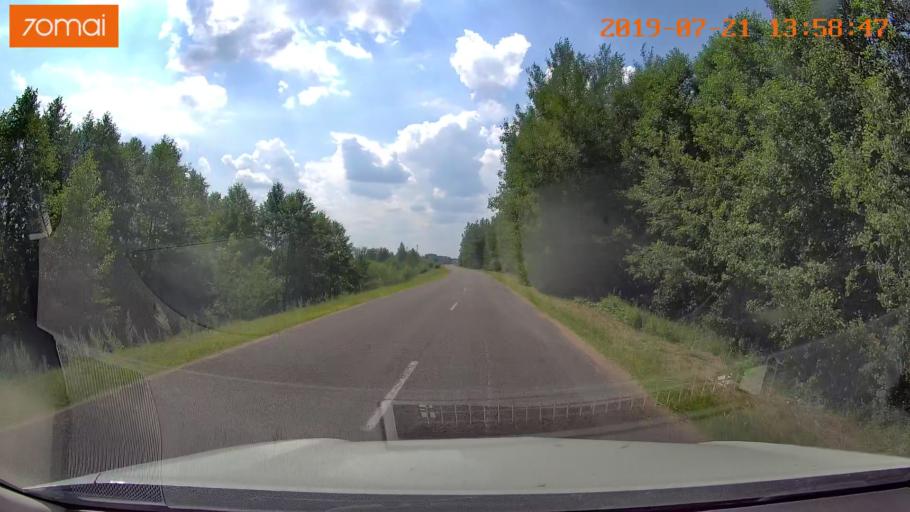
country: BY
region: Grodnenskaya
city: Lyubcha
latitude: 53.7584
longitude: 26.0731
